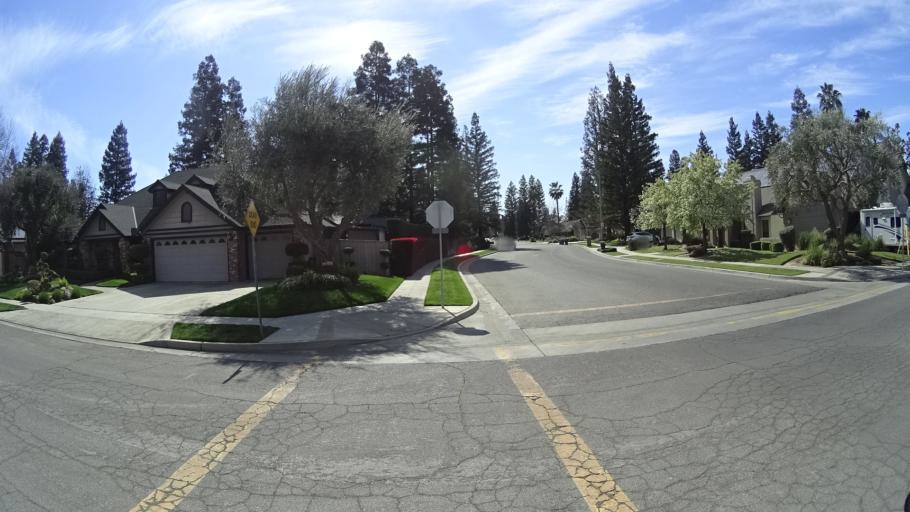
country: US
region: California
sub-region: Fresno County
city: Clovis
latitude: 36.8593
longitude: -119.7696
